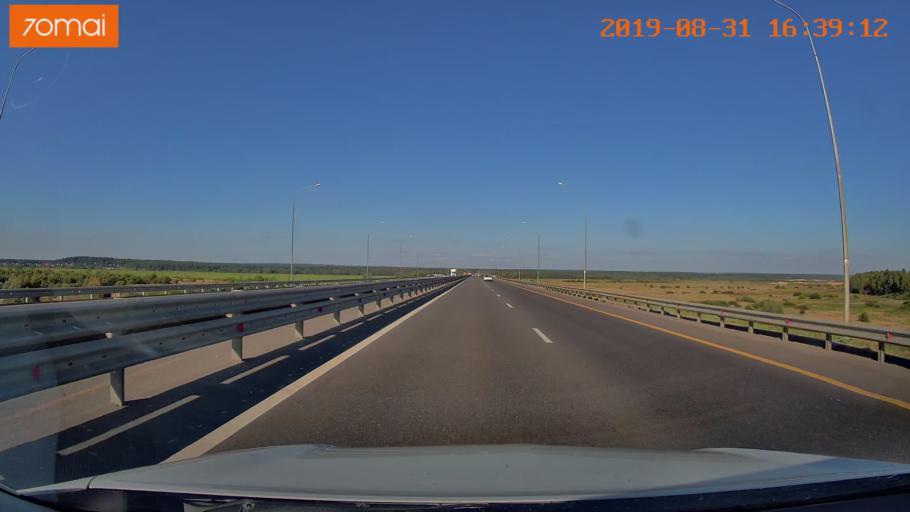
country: RU
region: Kaluga
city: Kurovskoye
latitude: 54.5490
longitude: 36.0224
